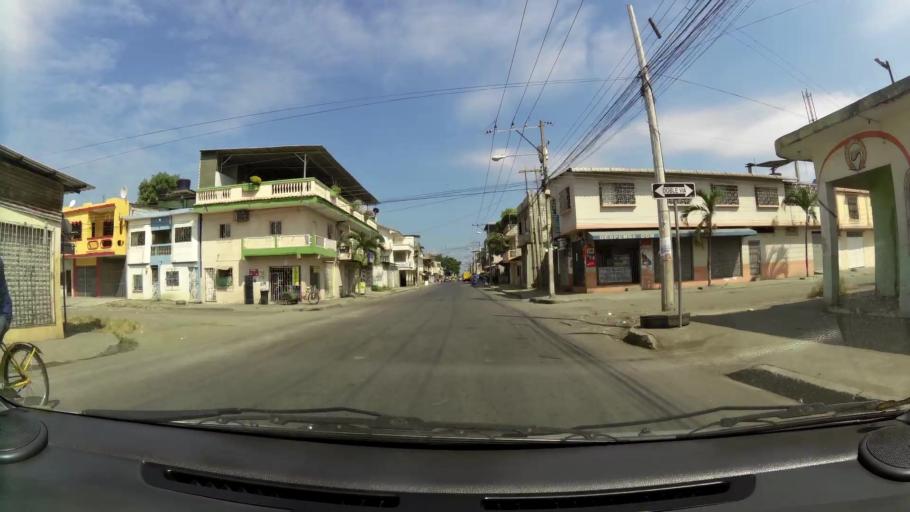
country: EC
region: Guayas
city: Guayaquil
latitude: -2.2672
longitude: -79.8796
